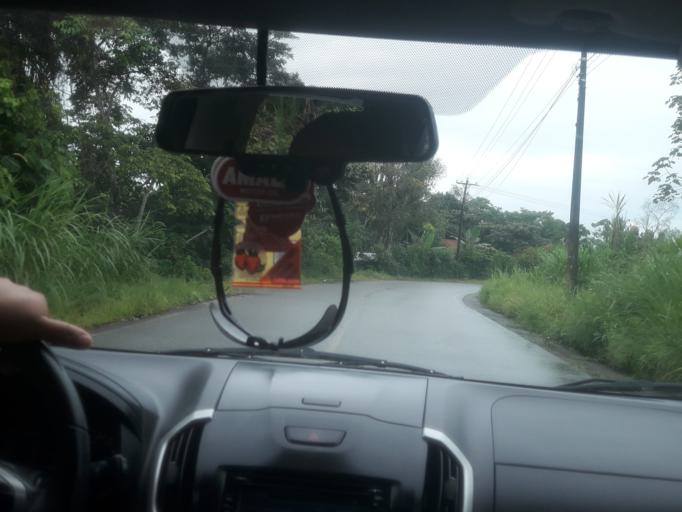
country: EC
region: Napo
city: Tena
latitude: -1.0298
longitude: -77.7416
